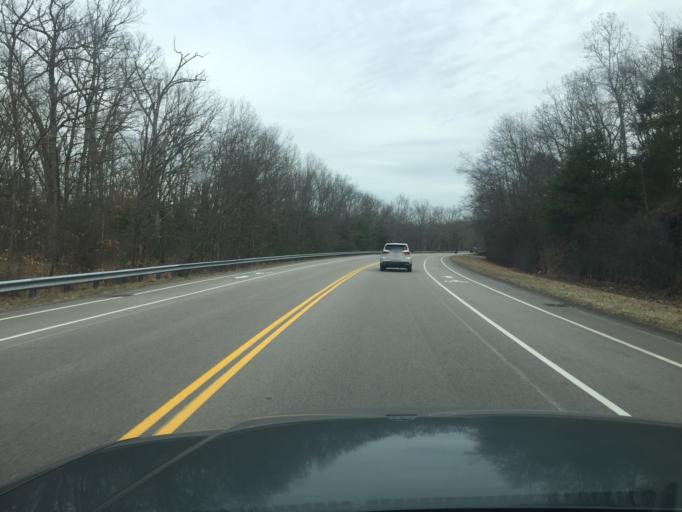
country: US
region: Massachusetts
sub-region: Middlesex County
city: Sherborn
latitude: 42.2086
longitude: -71.3426
